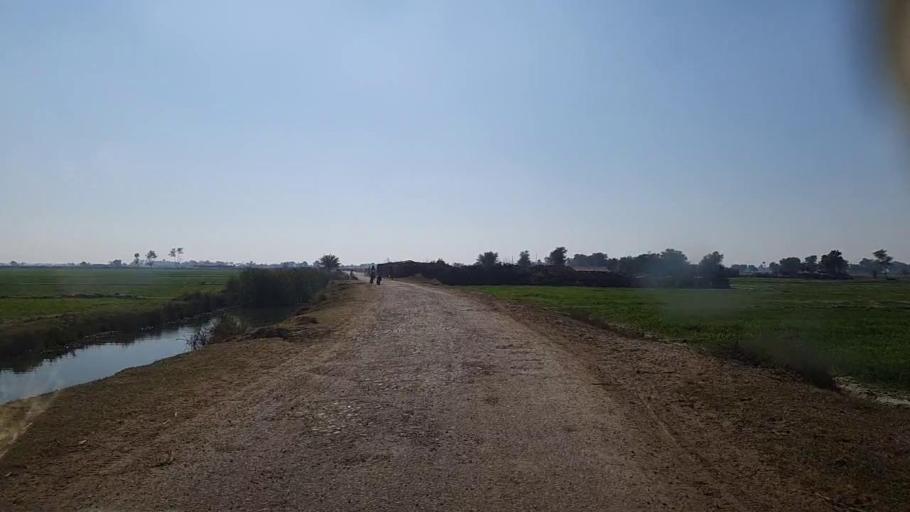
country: PK
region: Sindh
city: Khairpur
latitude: 28.0390
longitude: 69.7825
